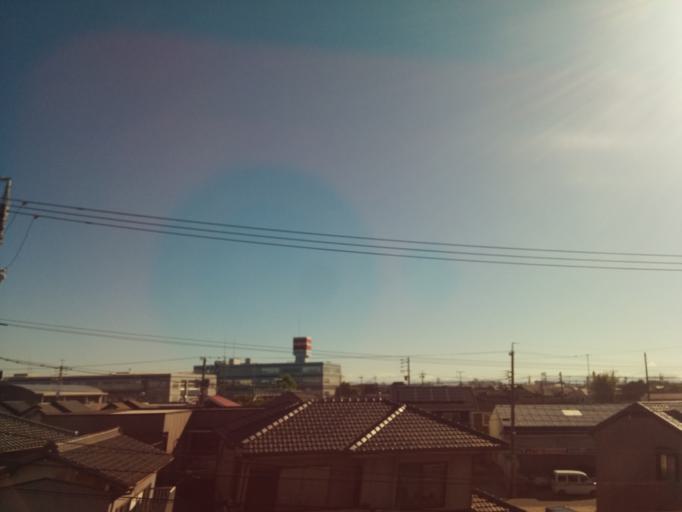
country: JP
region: Aichi
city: Inazawa
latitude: 35.2209
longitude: 136.8365
